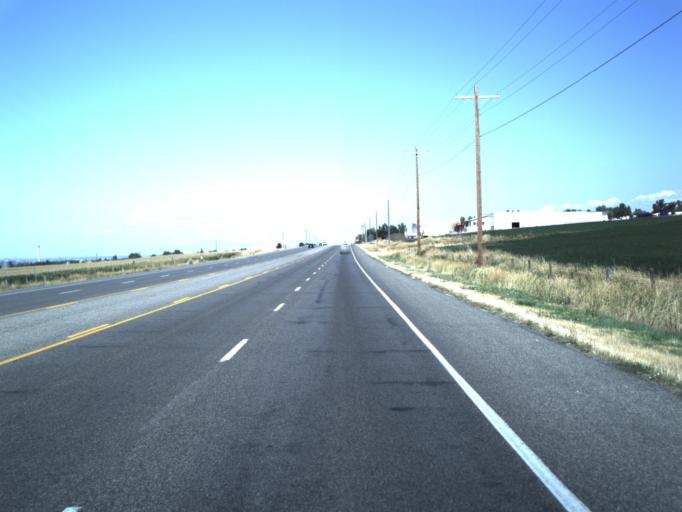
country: US
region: Utah
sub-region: Cache County
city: Richmond
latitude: 41.9016
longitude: -111.8147
